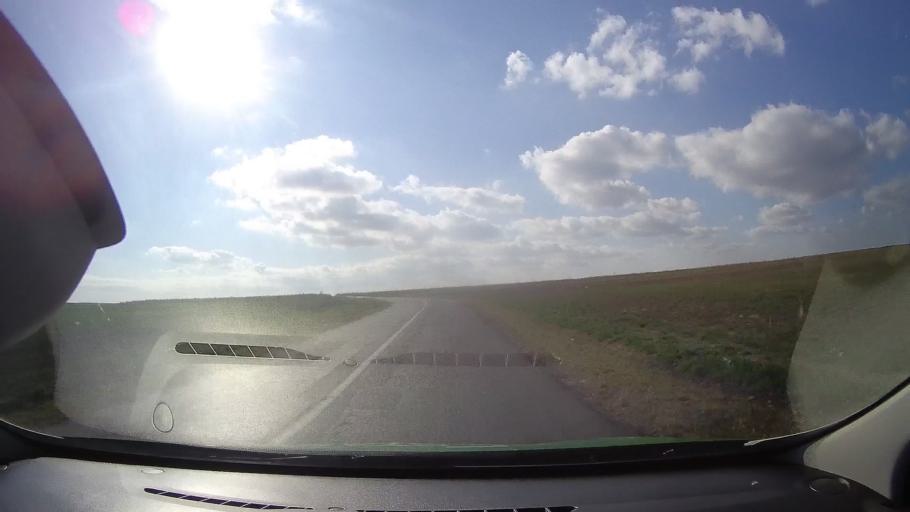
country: RO
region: Constanta
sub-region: Comuna Mihai Viteazu
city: Mihai Viteazu
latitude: 44.6207
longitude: 28.7276
